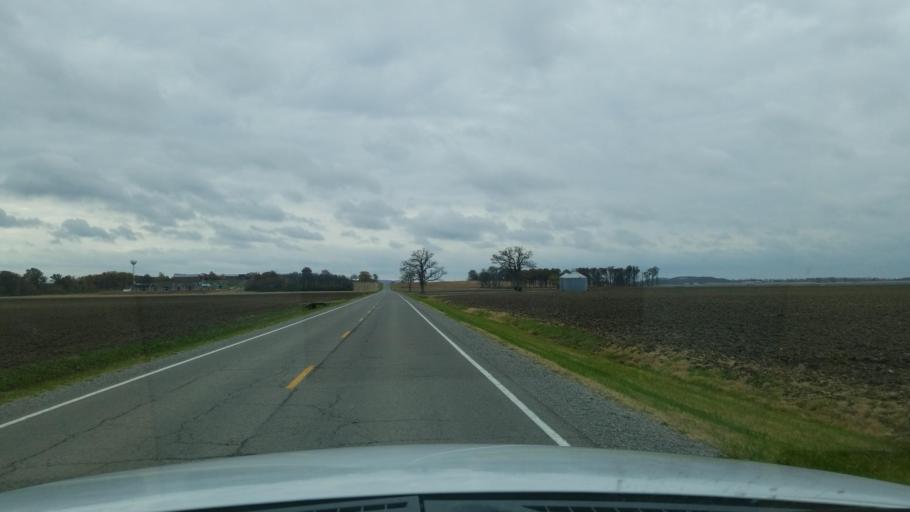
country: US
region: Illinois
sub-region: Saline County
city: Eldorado
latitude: 37.7632
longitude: -88.4383
